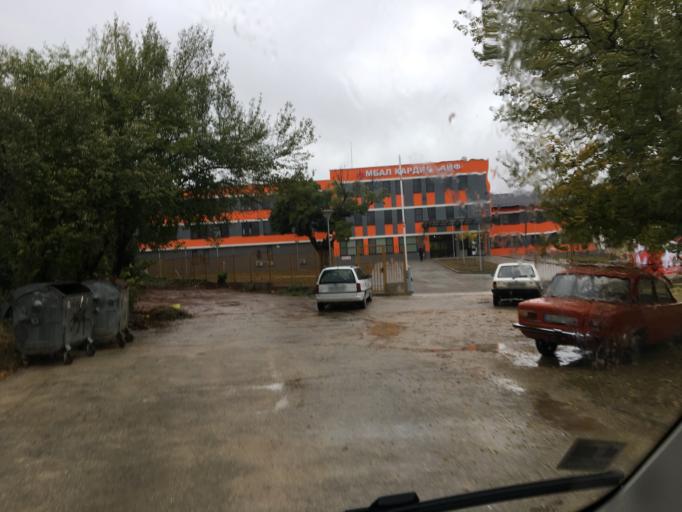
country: BG
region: Lovech
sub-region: Obshtina Lovech
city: Lovech
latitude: 43.1598
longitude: 24.7138
